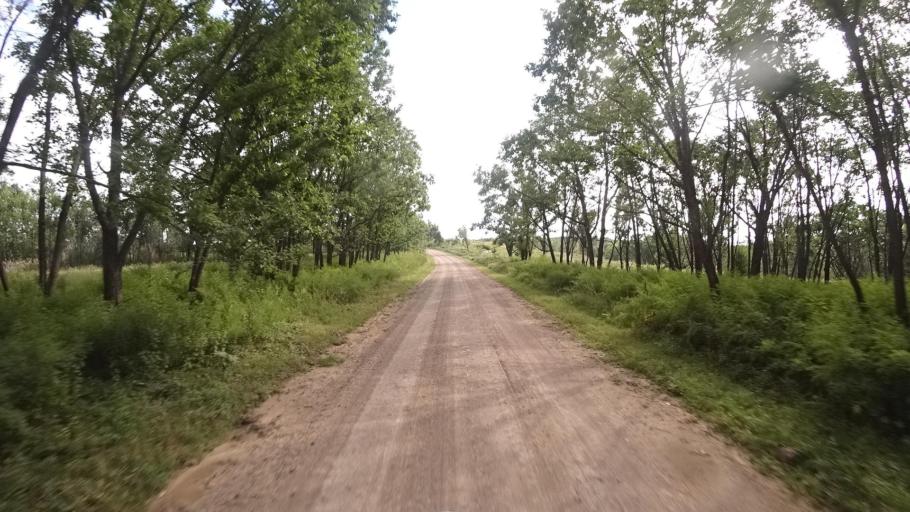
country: RU
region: Primorskiy
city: Dostoyevka
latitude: 44.3610
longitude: 133.5217
